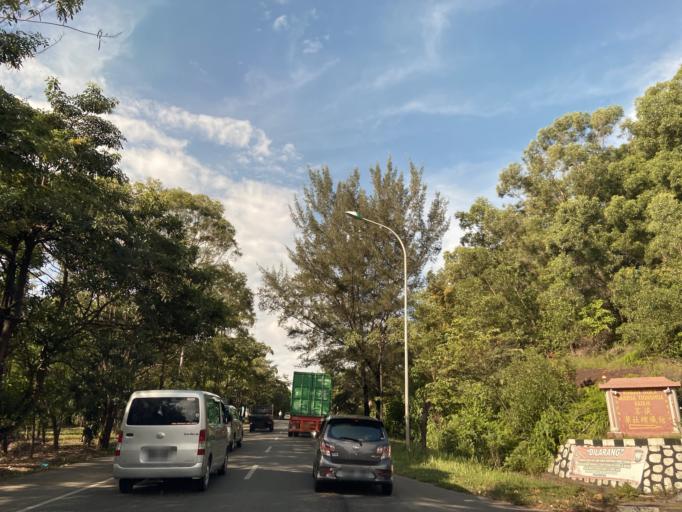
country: SG
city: Singapore
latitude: 1.1216
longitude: 104.0068
